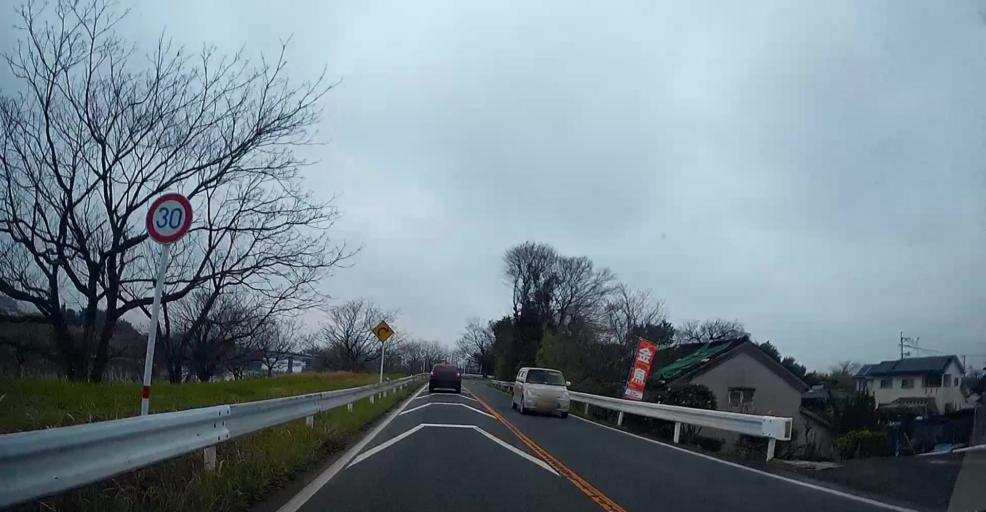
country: JP
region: Kumamoto
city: Kumamoto
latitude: 32.7537
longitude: 130.7424
